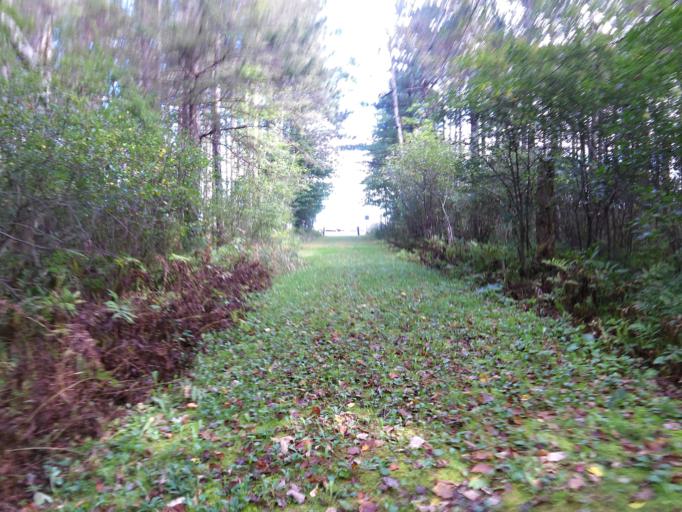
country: CA
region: Ontario
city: Ottawa
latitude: 45.3508
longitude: -75.5855
